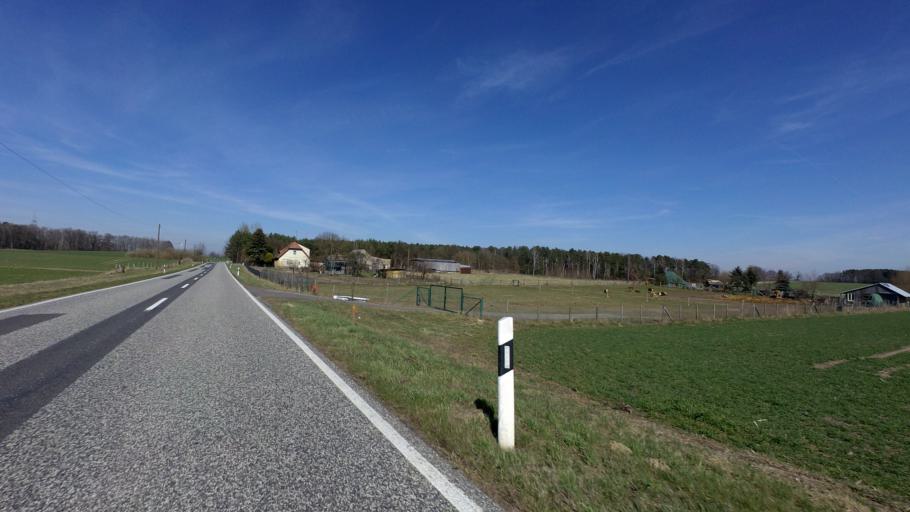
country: DE
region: Brandenburg
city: Furstenwalde
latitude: 52.4139
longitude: 14.0459
